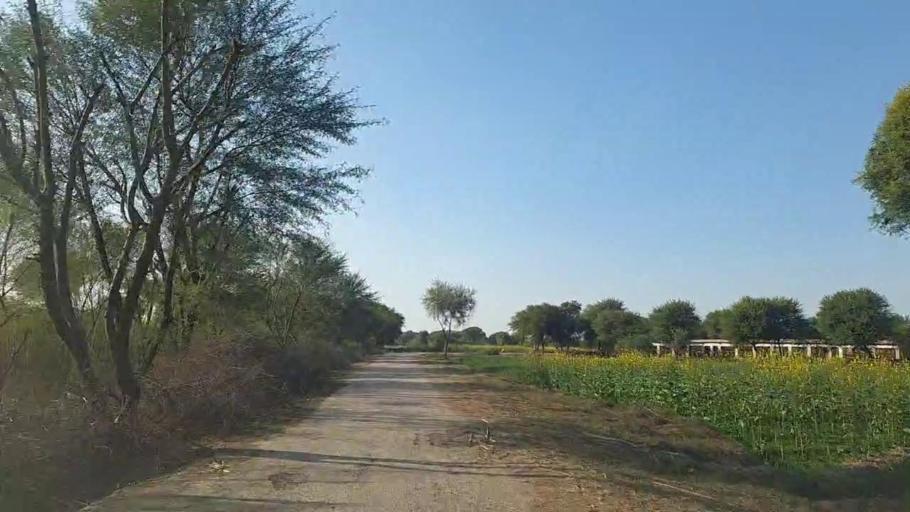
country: PK
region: Sindh
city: Shahpur Chakar
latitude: 26.1944
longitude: 68.6343
